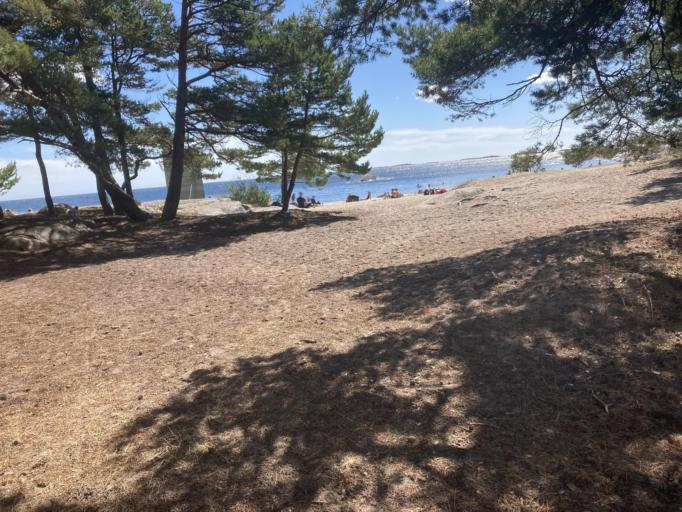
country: SE
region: Stockholm
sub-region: Varmdo Kommun
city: Holo
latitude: 59.2739
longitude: 18.9242
